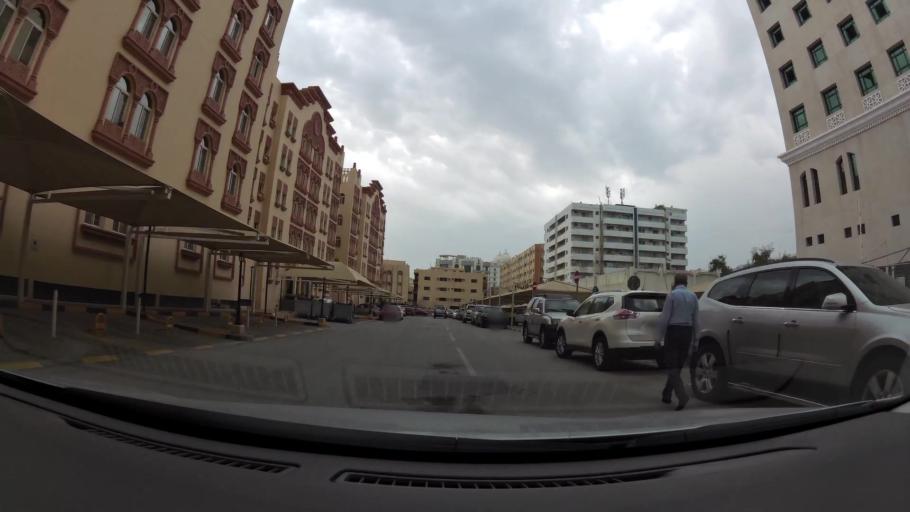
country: QA
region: Baladiyat ad Dawhah
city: Doha
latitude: 25.2803
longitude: 51.5048
